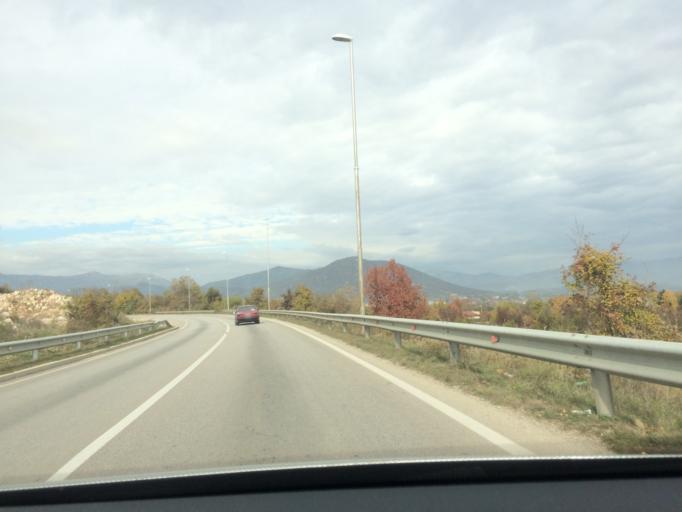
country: ME
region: Opstina Niksic
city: Niksic
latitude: 42.7796
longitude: 18.9351
